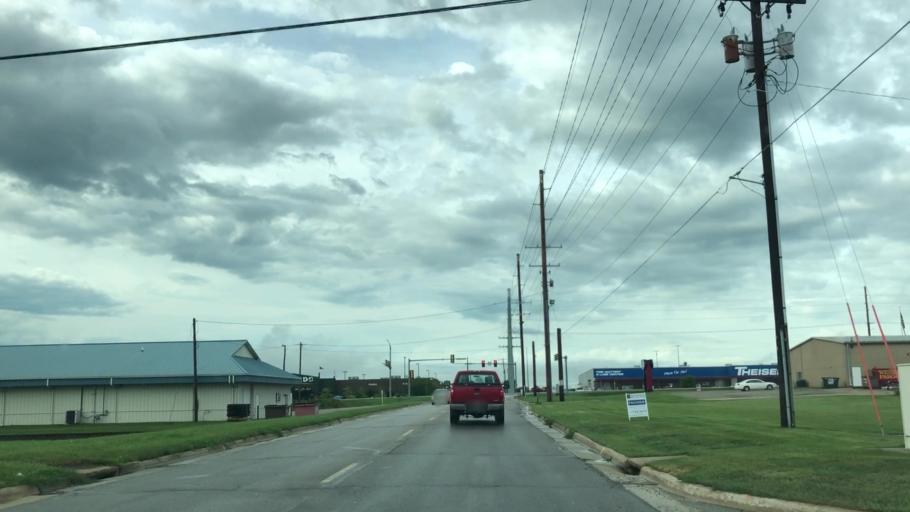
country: US
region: Iowa
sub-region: Marshall County
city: Marshalltown
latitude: 42.0085
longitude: -92.9222
